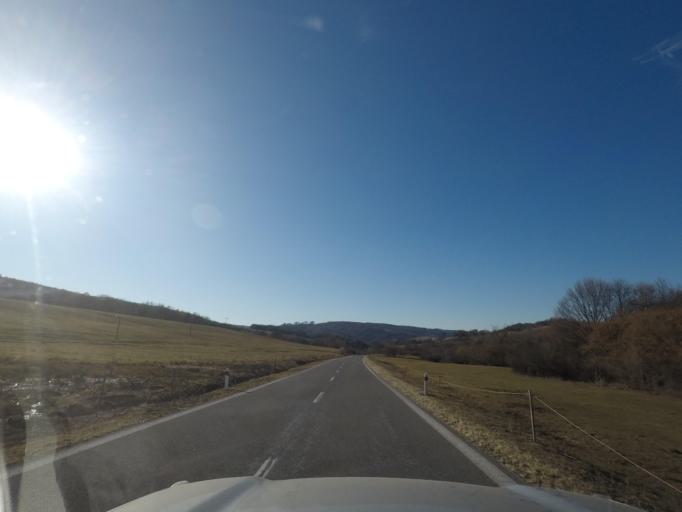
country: PL
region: Subcarpathian Voivodeship
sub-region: Powiat sanocki
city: Komancza
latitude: 49.1590
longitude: 22.0526
